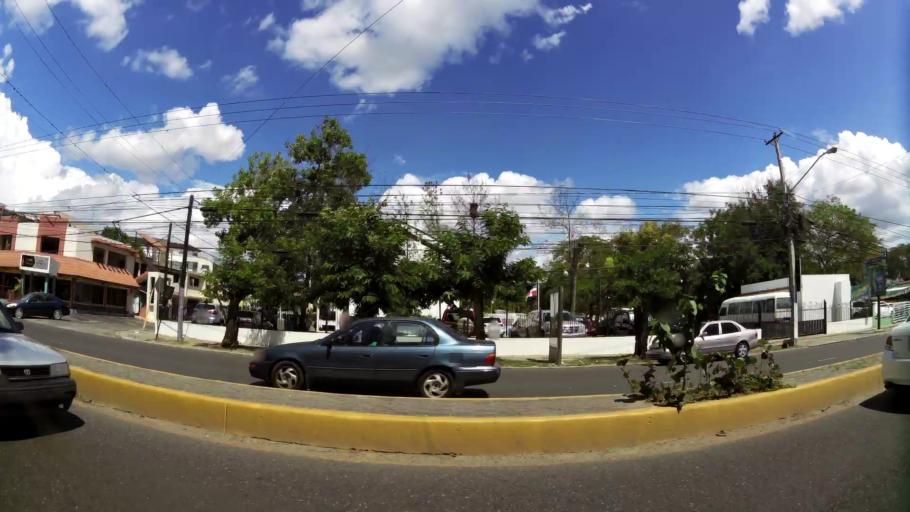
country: DO
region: Santiago
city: Santiago de los Caballeros
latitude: 19.4451
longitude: -70.6877
